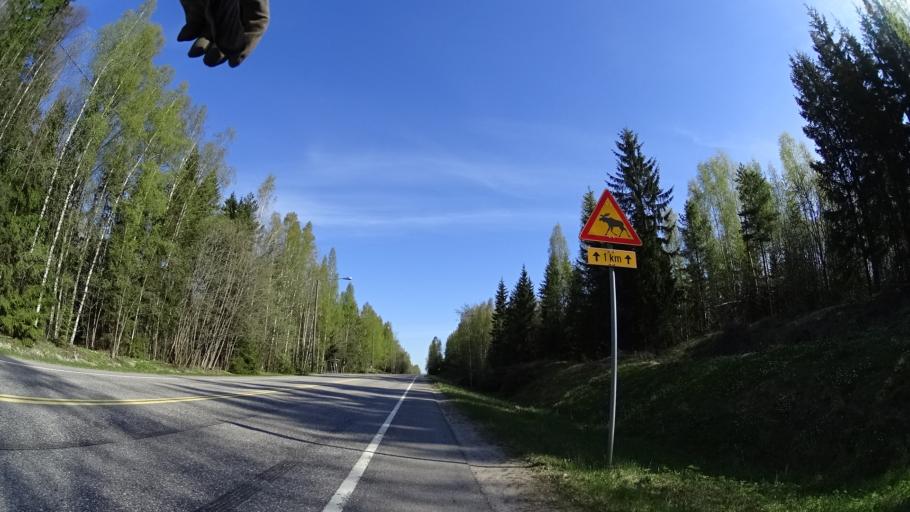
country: FI
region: Uusimaa
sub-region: Helsinki
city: Nurmijaervi
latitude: 60.3731
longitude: 24.8056
